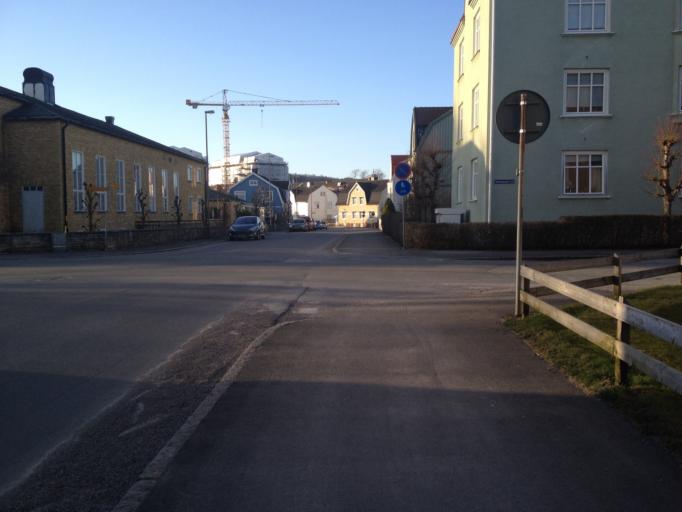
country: SE
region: Vaestra Goetaland
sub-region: Falkopings Kommun
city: Falkoeping
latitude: 58.1719
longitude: 13.5542
